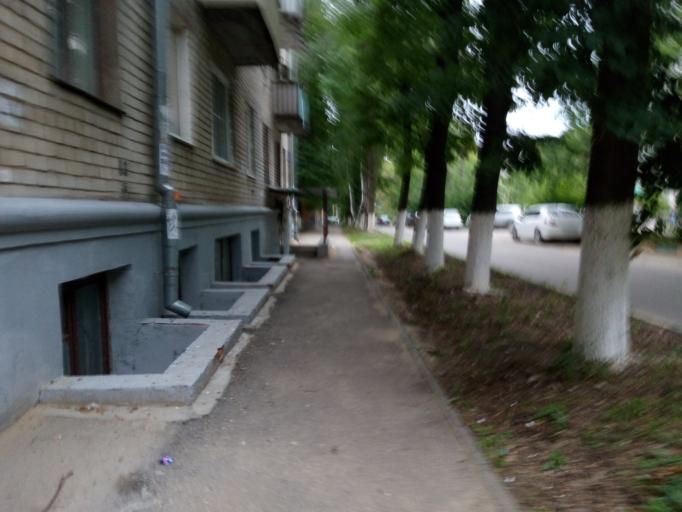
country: RU
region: Nizjnij Novgorod
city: Nizhniy Novgorod
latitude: 56.2718
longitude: 43.9790
